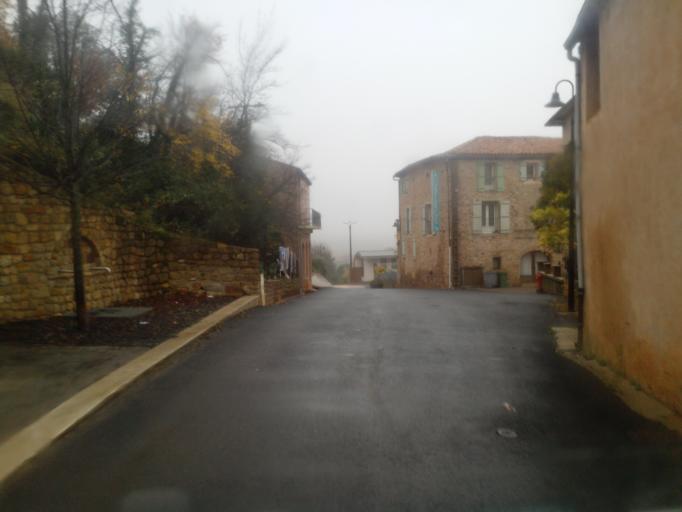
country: FR
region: Languedoc-Roussillon
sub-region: Departement de l'Herault
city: Nebian
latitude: 43.6355
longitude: 3.3703
